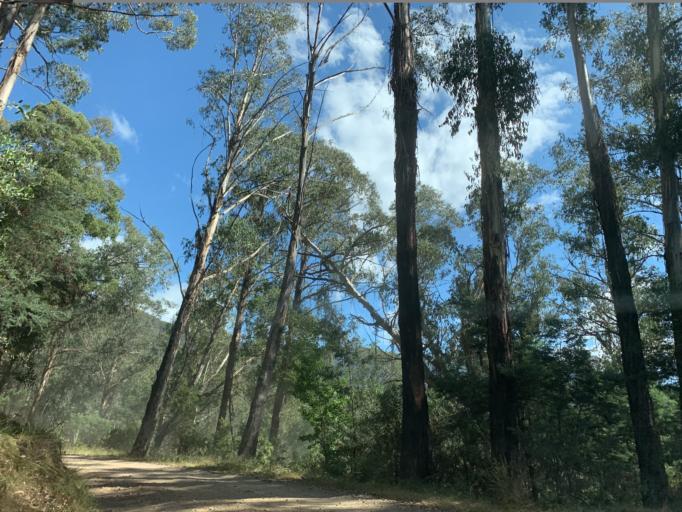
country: AU
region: Victoria
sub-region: Mansfield
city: Mansfield
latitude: -37.0910
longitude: 146.5155
